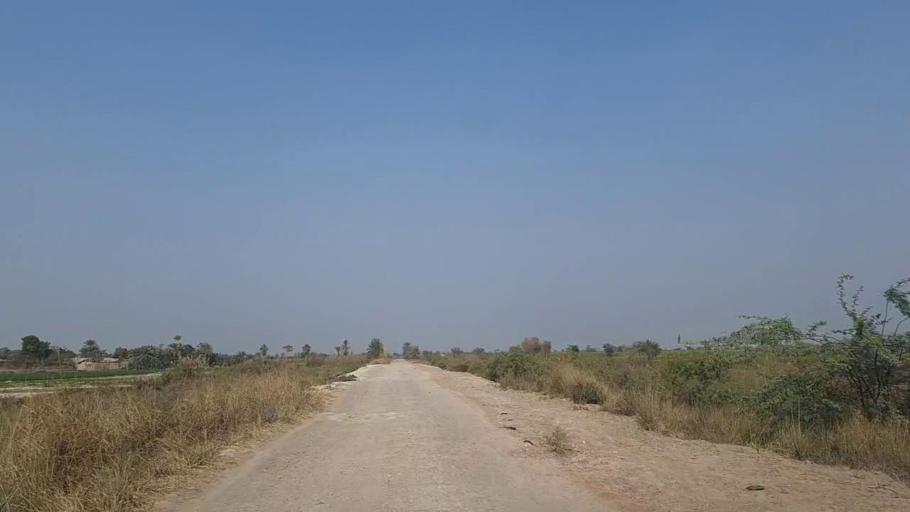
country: PK
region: Sindh
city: Daur
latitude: 26.4808
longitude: 68.4513
